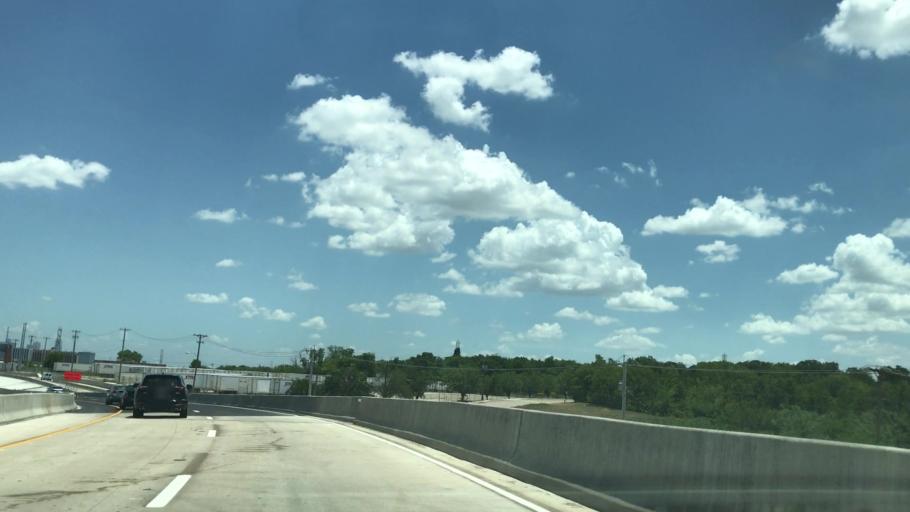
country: US
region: Texas
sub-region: Dallas County
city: Irving
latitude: 32.8364
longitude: -96.9038
